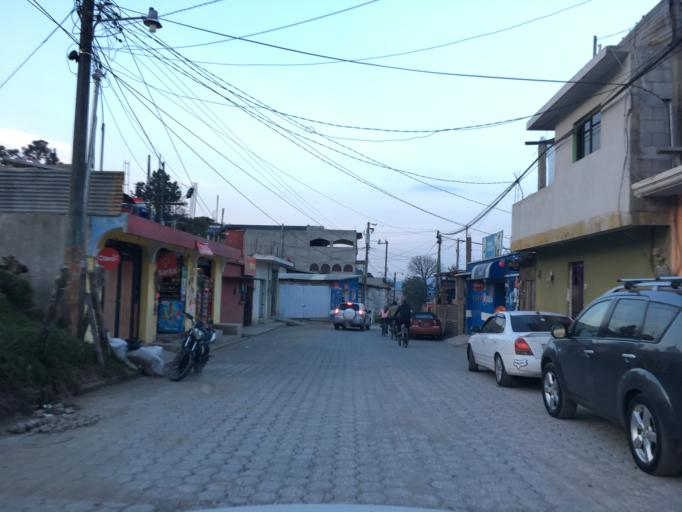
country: GT
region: Chimaltenango
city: Tecpan Guatemala
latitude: 14.7585
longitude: -91.0002
